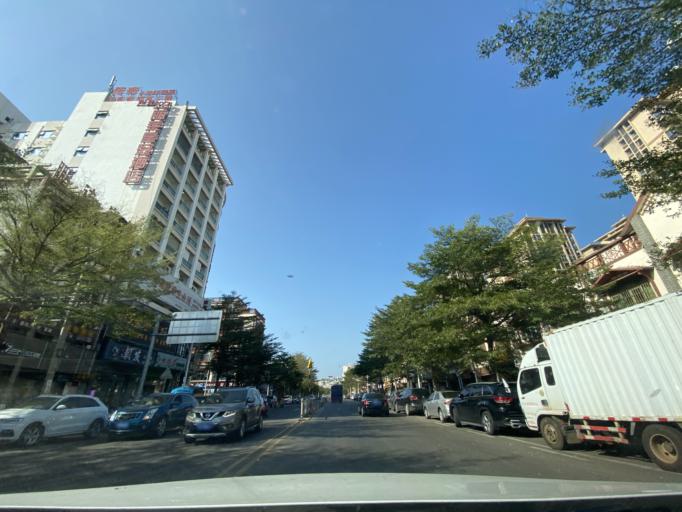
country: CN
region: Hainan
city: Yingzhou
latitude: 18.4248
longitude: 109.8551
